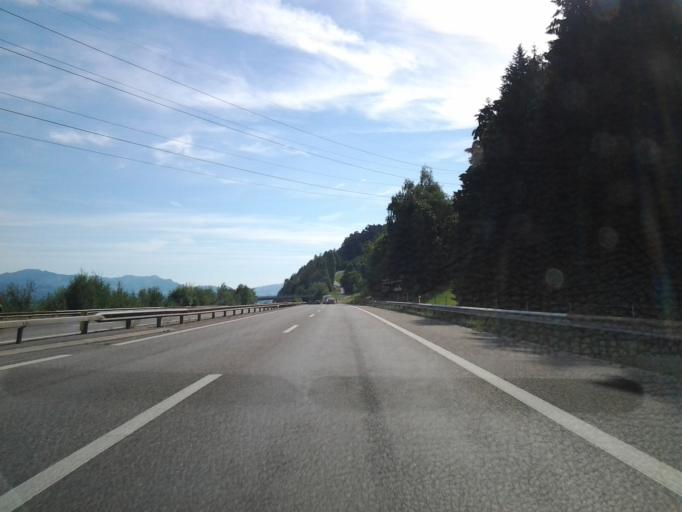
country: CH
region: Schwyz
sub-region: Bezirk Hoefe
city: Freienbach
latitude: 47.1944
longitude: 8.7739
